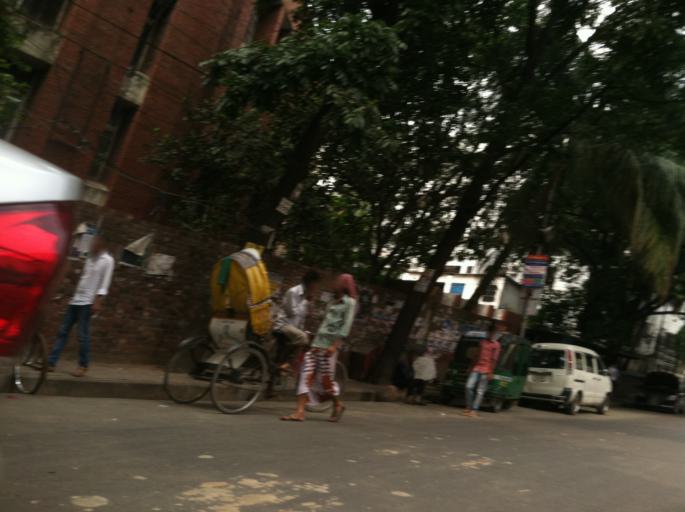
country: BD
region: Dhaka
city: Paltan
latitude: 23.7880
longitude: 90.4007
